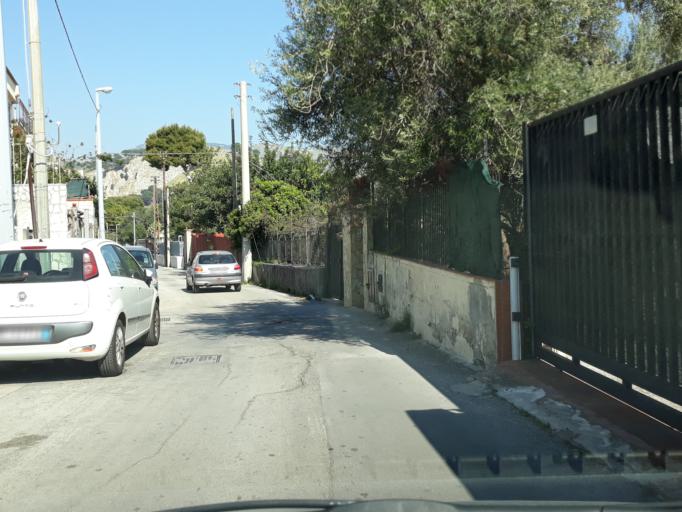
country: IT
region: Sicily
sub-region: Palermo
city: Piano dei Geli
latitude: 38.1119
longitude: 13.2982
